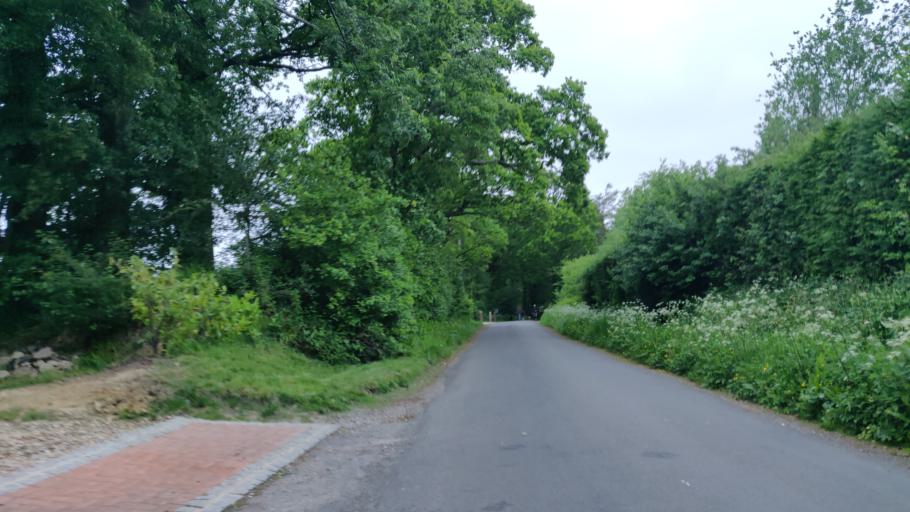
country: GB
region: England
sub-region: West Sussex
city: Southwater
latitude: 51.0371
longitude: -0.3356
